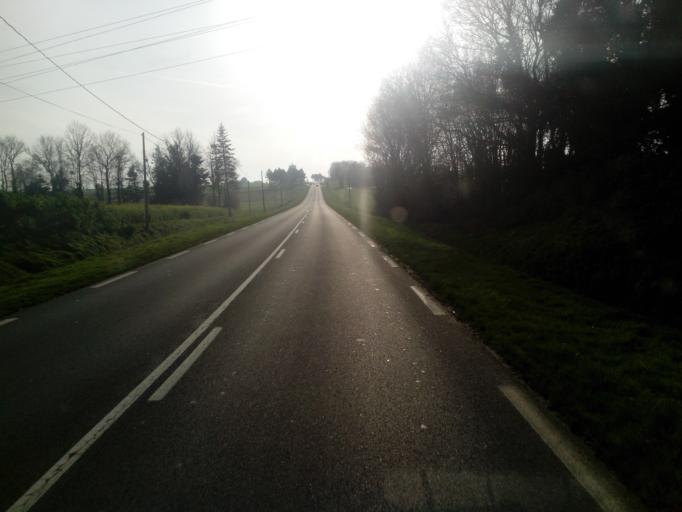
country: FR
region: Brittany
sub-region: Departement d'Ille-et-Vilaine
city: Gael
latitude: 48.1507
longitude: -2.2149
